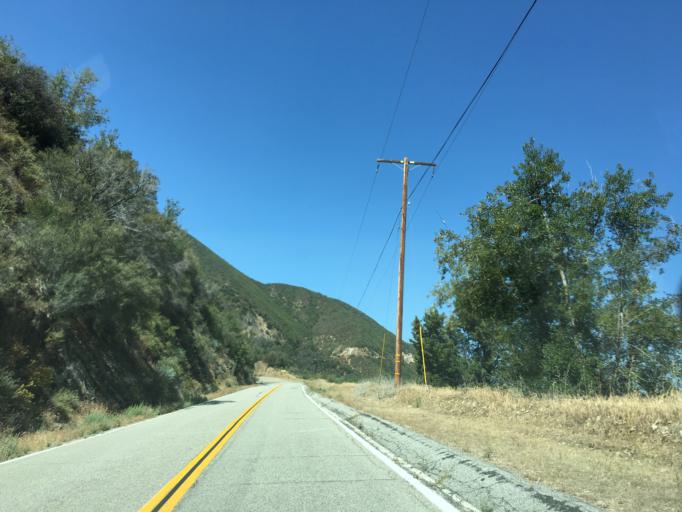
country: US
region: California
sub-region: Los Angeles County
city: San Dimas
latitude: 34.2296
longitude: -117.7751
